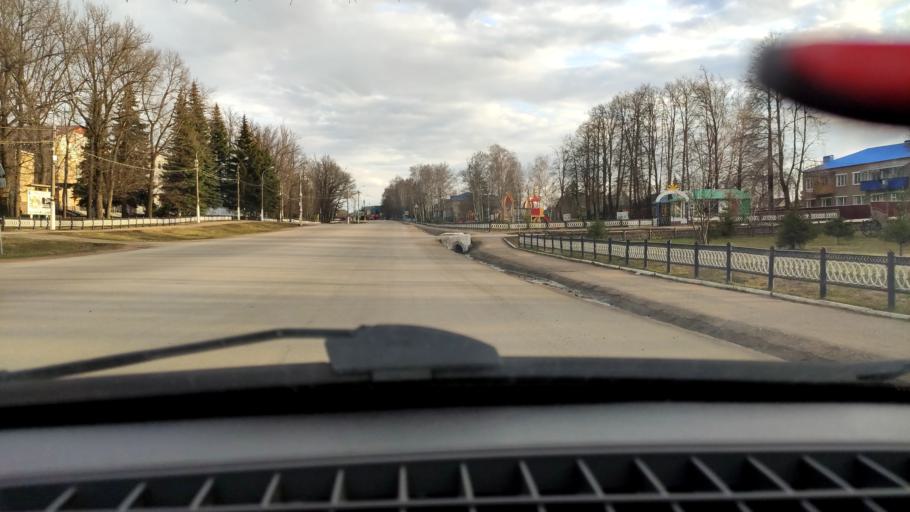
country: RU
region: Bashkortostan
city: Tolbazy
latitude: 54.0145
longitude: 55.8863
